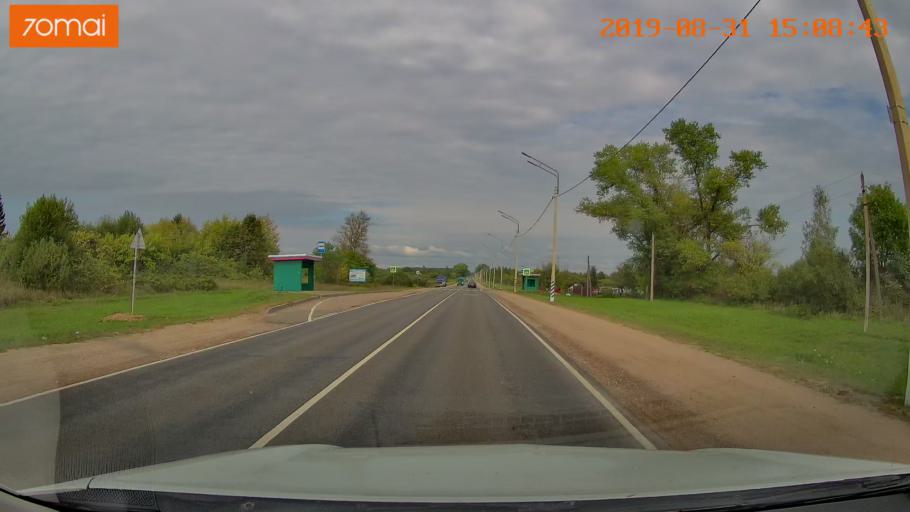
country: RU
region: Kaluga
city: Spas-Demensk
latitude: 54.3946
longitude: 34.1886
